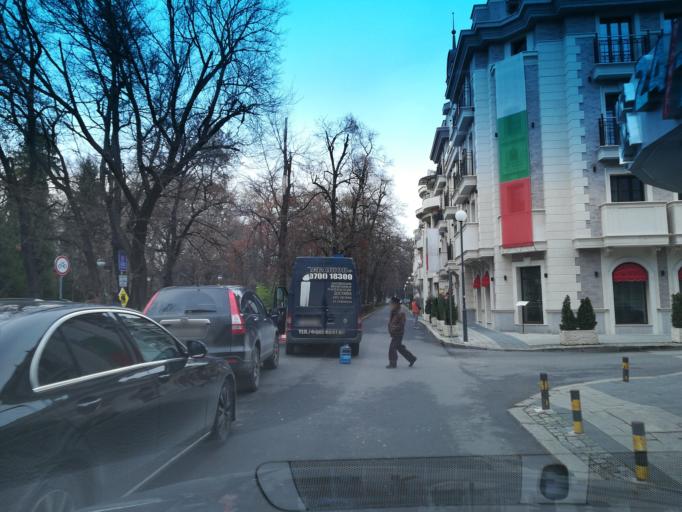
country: BG
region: Plovdiv
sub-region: Obshtina Plovdiv
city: Plovdiv
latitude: 42.1403
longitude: 24.7466
